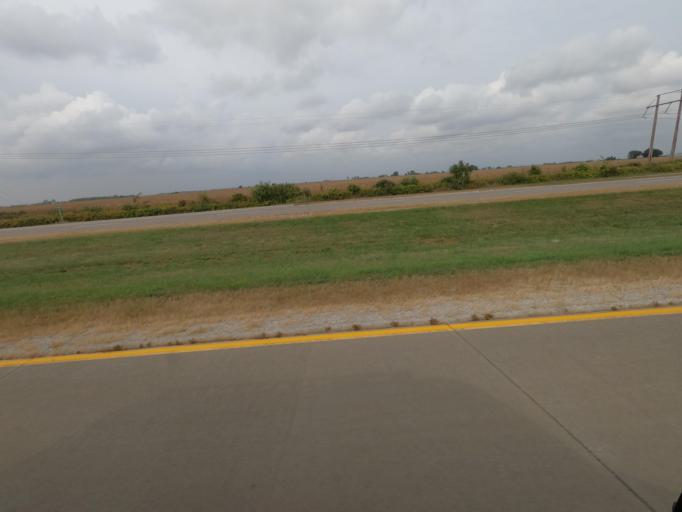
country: US
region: Iowa
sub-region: Wapello County
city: Ottumwa
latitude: 41.0913
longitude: -92.4154
